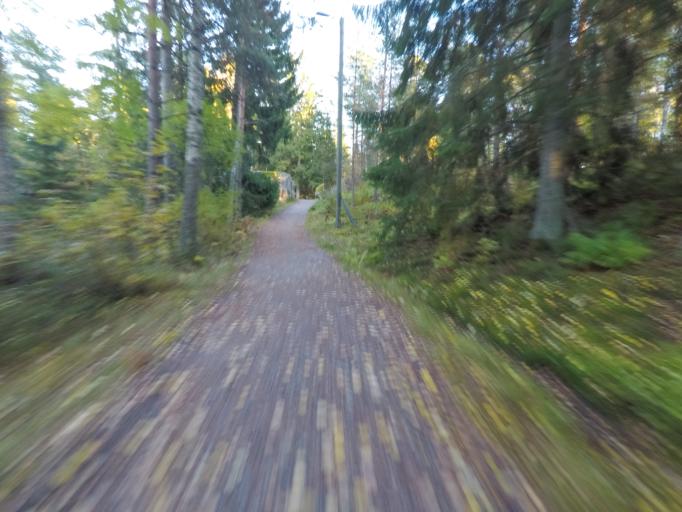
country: FI
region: Uusimaa
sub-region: Helsinki
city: Vantaa
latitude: 60.1724
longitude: 25.0591
